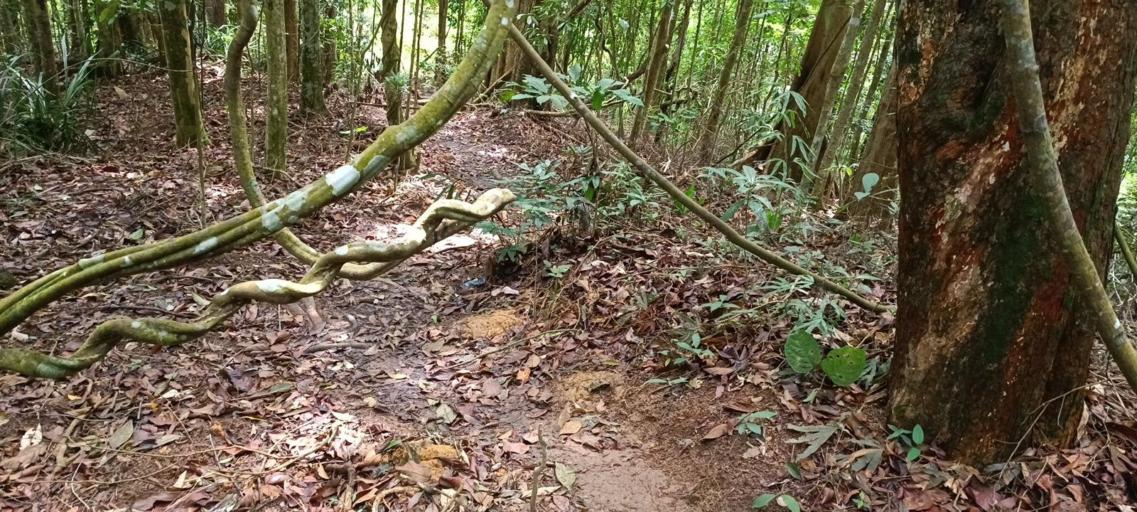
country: MY
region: Penang
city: Bukit Mertajam
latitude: 5.3728
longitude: 100.4853
